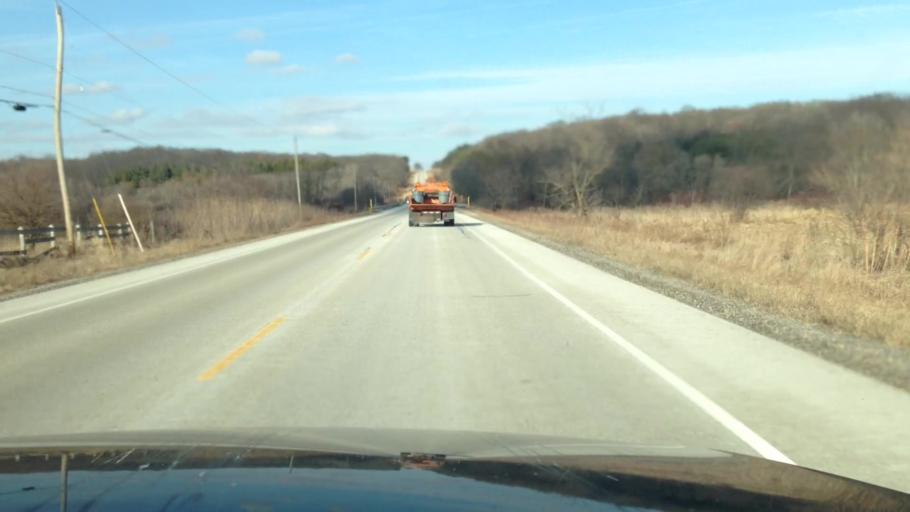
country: US
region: Wisconsin
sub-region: Walworth County
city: East Troy
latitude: 42.7294
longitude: -88.4057
